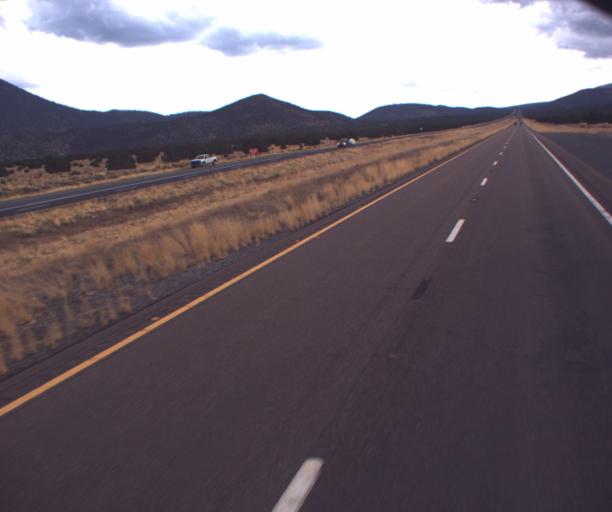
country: US
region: Arizona
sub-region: Coconino County
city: Flagstaff
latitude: 35.4415
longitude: -111.5657
